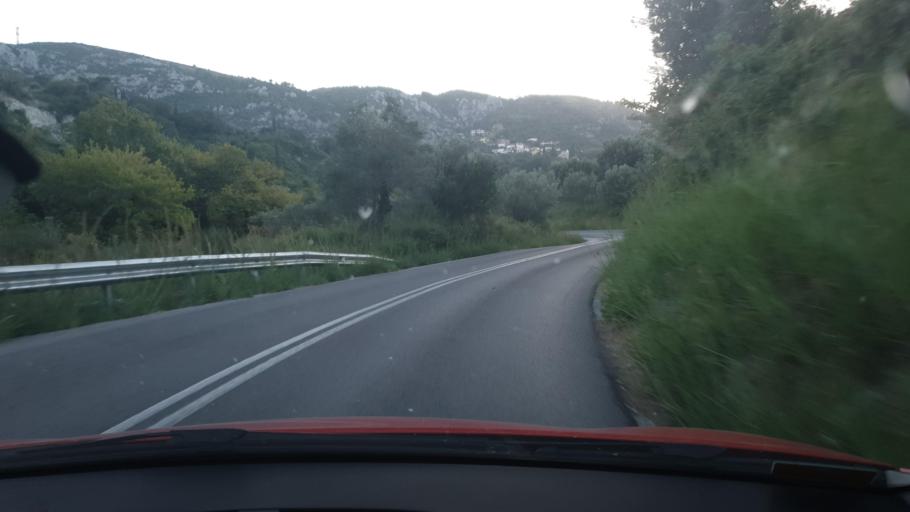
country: GR
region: Central Greece
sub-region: Nomos Evvoias
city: Kymi
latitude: 38.6298
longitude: 24.1183
